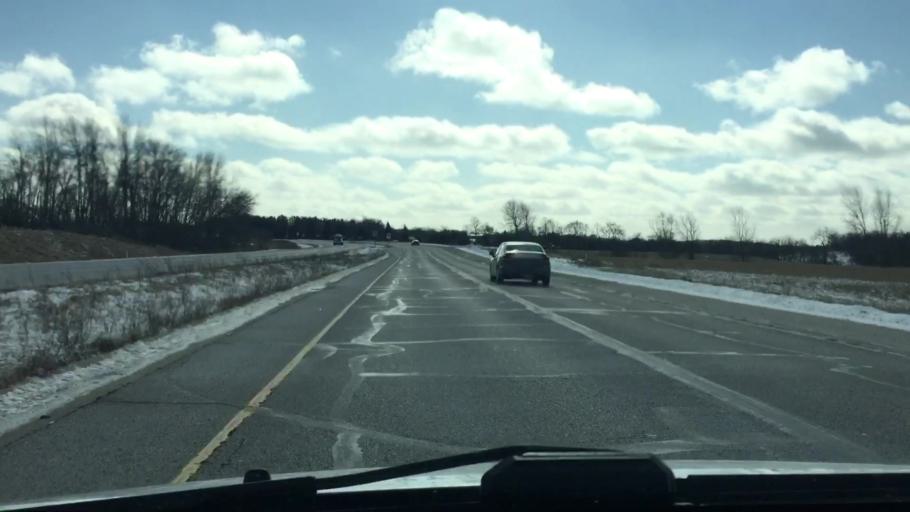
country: US
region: Wisconsin
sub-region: Waukesha County
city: Big Bend
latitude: 42.9279
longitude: -88.2288
